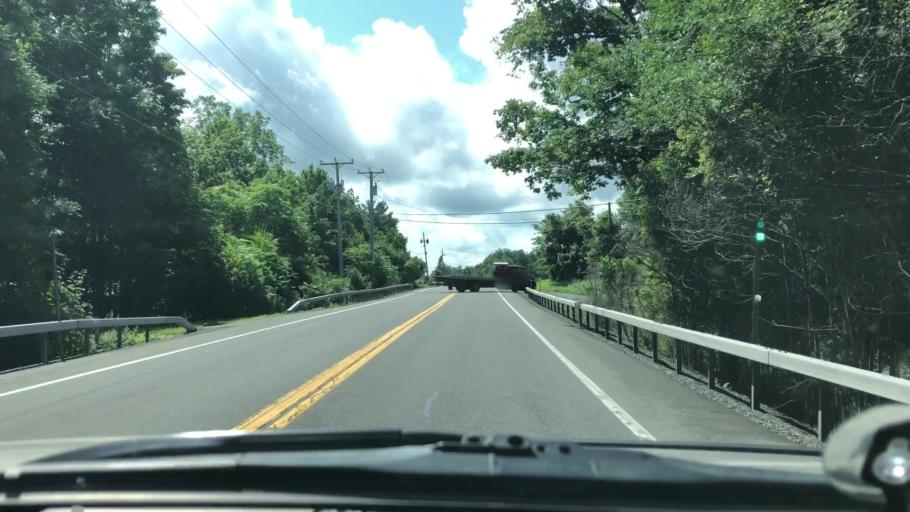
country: US
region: New York
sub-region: Greene County
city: Palenville
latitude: 42.2150
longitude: -73.9861
